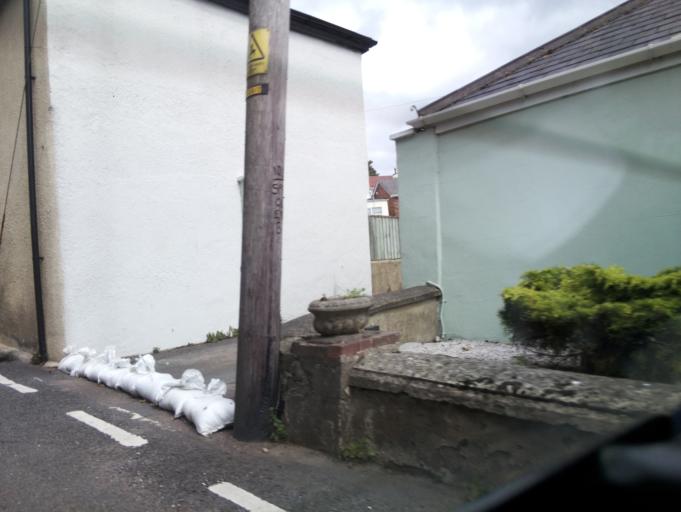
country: GB
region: England
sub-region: Devon
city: Dawlish
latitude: 50.5645
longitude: -3.4767
